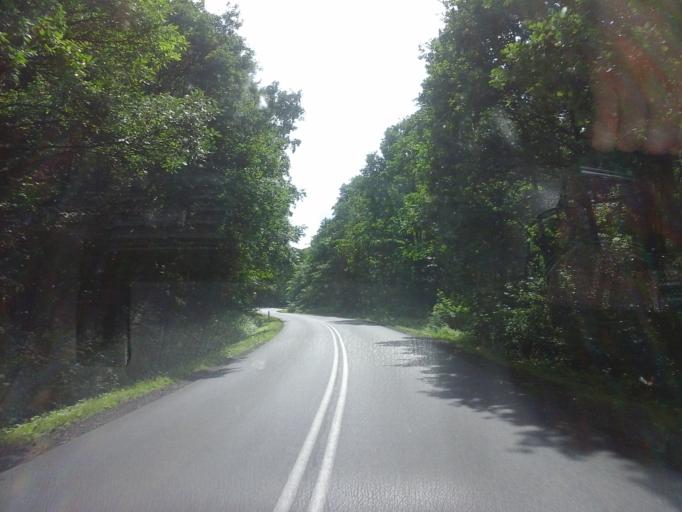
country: PL
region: West Pomeranian Voivodeship
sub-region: Powiat lobeski
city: Lobez
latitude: 53.6771
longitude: 15.6650
